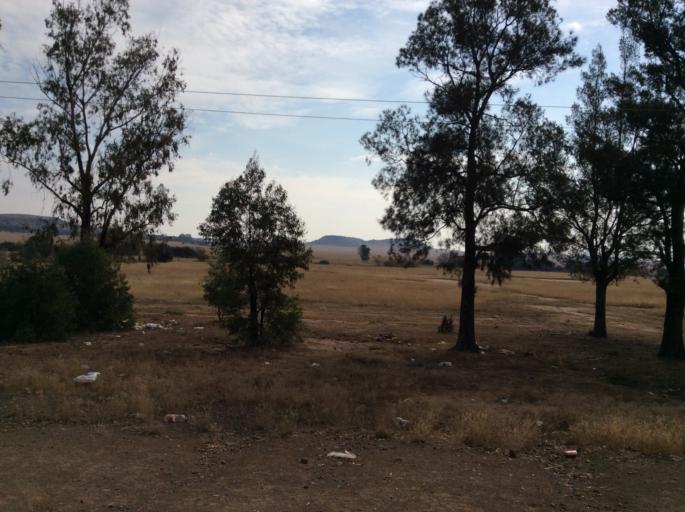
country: ZA
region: Orange Free State
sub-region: Xhariep District Municipality
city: Dewetsdorp
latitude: -29.5743
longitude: 26.6818
